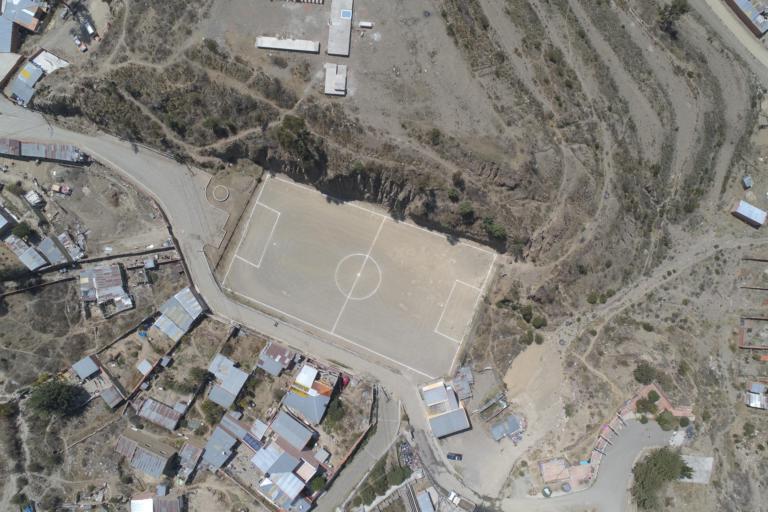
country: BO
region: La Paz
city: La Paz
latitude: -16.5002
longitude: -68.0988
